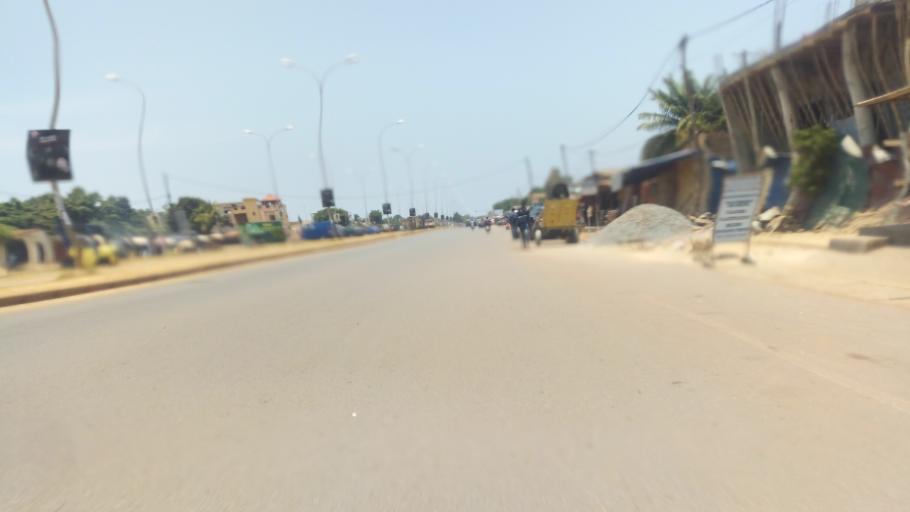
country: TG
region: Maritime
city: Lome
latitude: 6.2293
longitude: 1.1949
